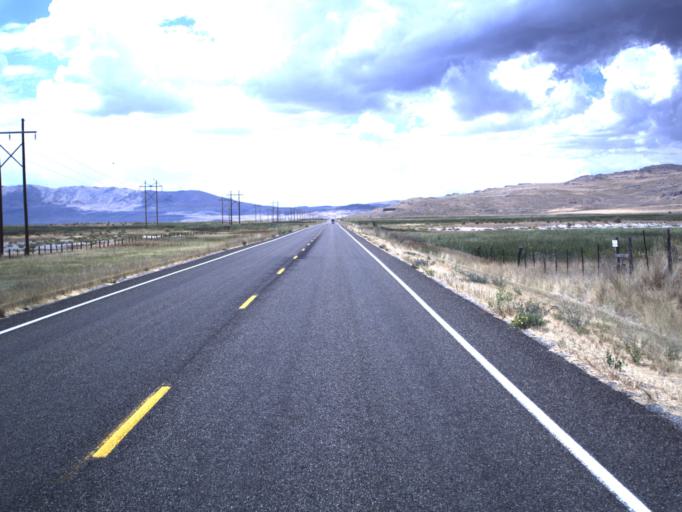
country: US
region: Utah
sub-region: Box Elder County
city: Tremonton
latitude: 41.6095
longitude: -112.3373
